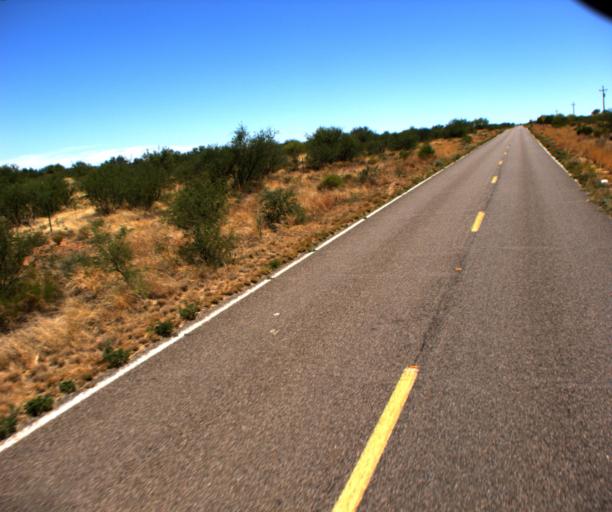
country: US
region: Arizona
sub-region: Pima County
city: Three Points
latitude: 31.7656
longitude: -111.4715
